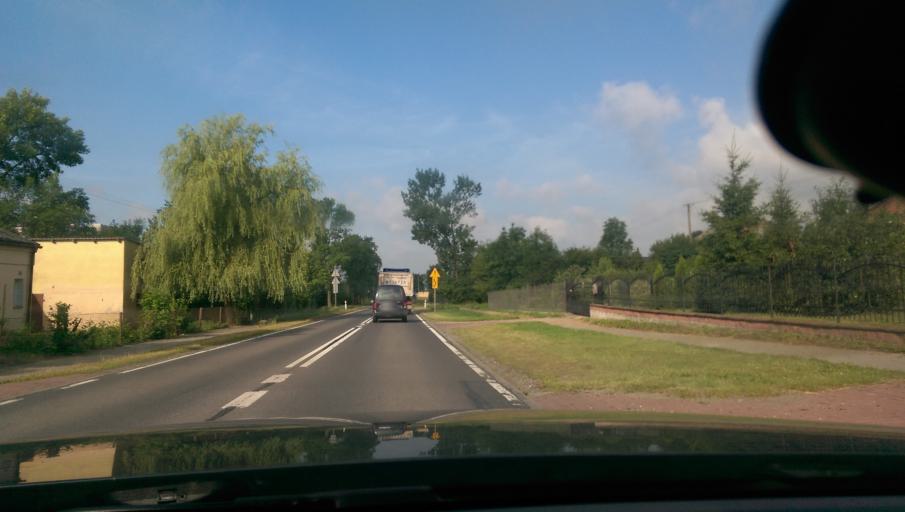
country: PL
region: Masovian Voivodeship
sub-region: Powiat ciechanowski
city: Opinogora Gorna
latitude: 52.9295
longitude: 20.6956
